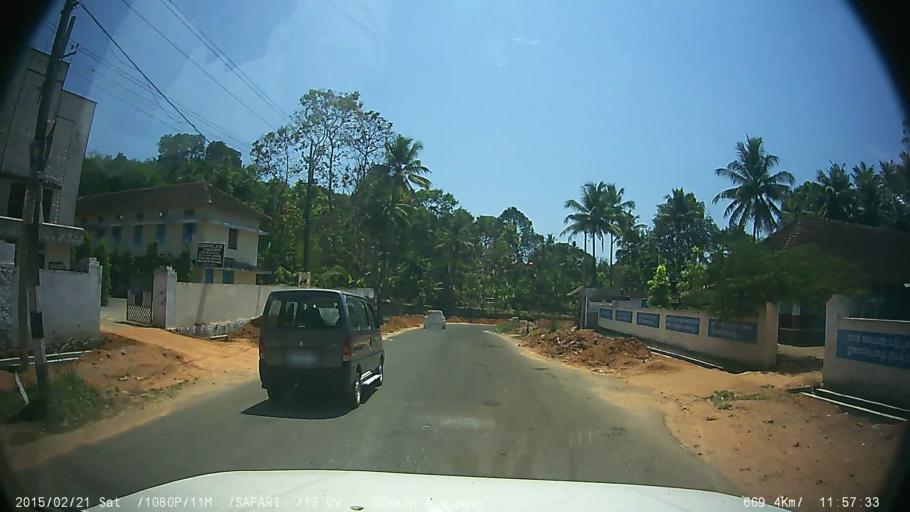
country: IN
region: Kerala
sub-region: Kottayam
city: Lalam
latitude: 9.7386
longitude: 76.6909
